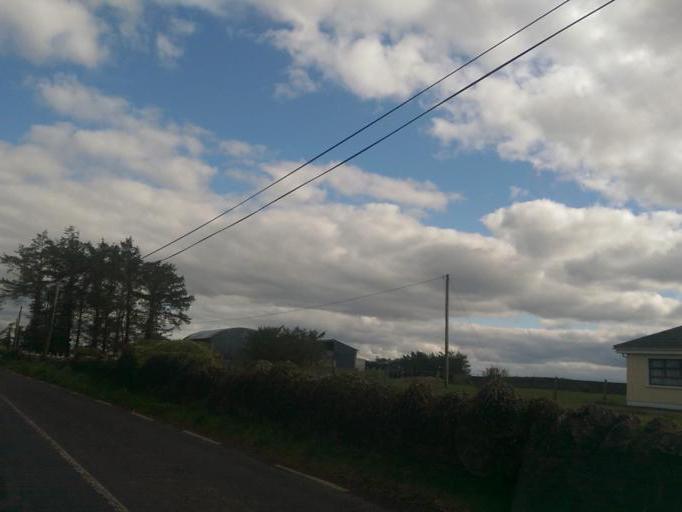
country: IE
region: Connaught
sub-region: County Galway
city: Loughrea
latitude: 53.4200
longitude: -8.5248
